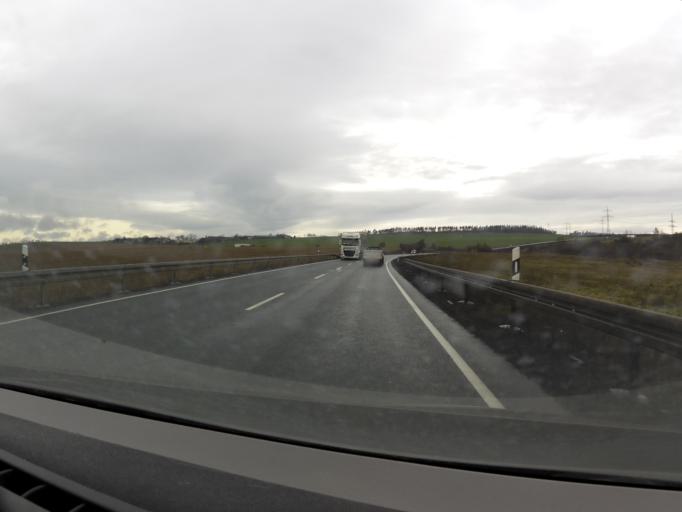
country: DE
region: Saxony-Anhalt
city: Grossorner
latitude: 51.6125
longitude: 11.4729
